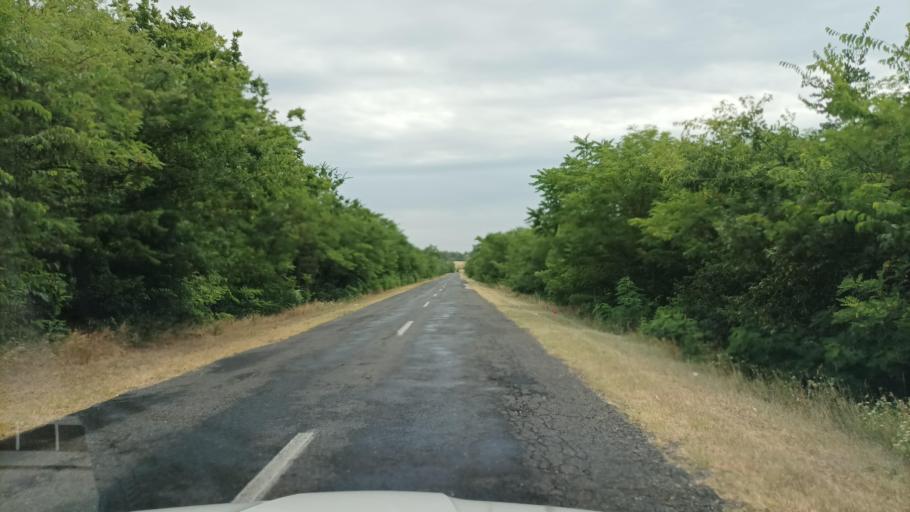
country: HU
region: Pest
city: Dabas
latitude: 47.1281
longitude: 19.3447
